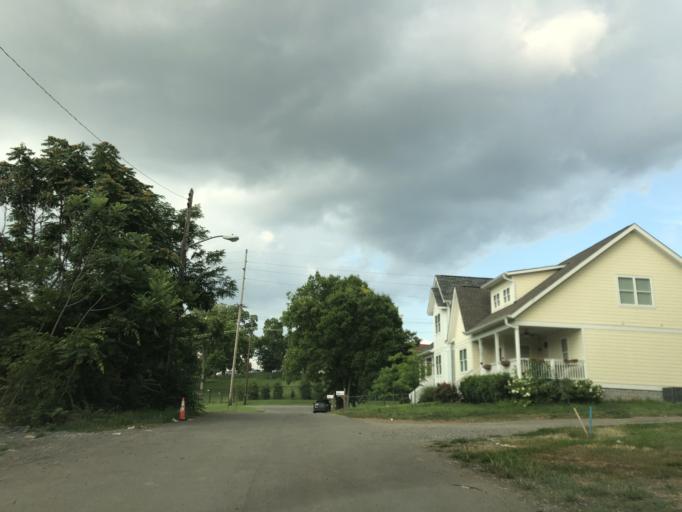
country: US
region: Tennessee
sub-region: Davidson County
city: Nashville
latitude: 36.1858
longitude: -86.8033
